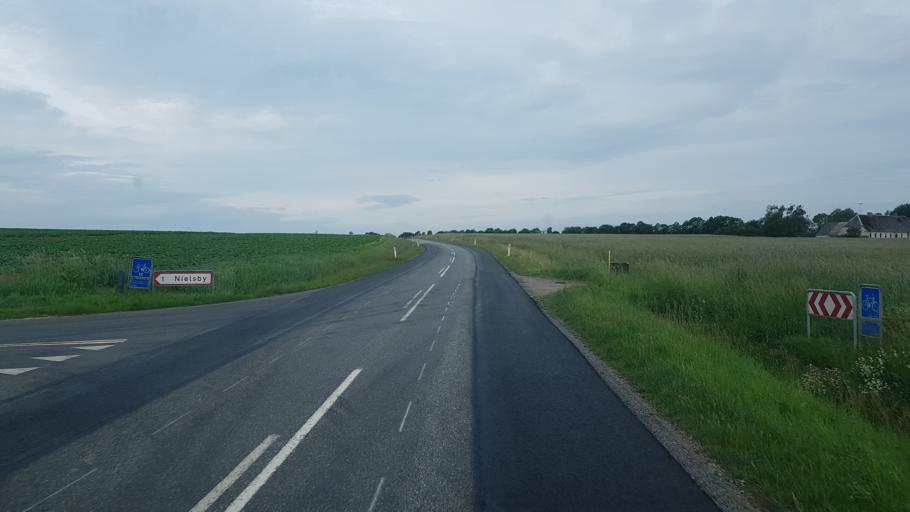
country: DK
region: South Denmark
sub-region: Vejen Kommune
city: Holsted
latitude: 55.4413
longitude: 8.9494
